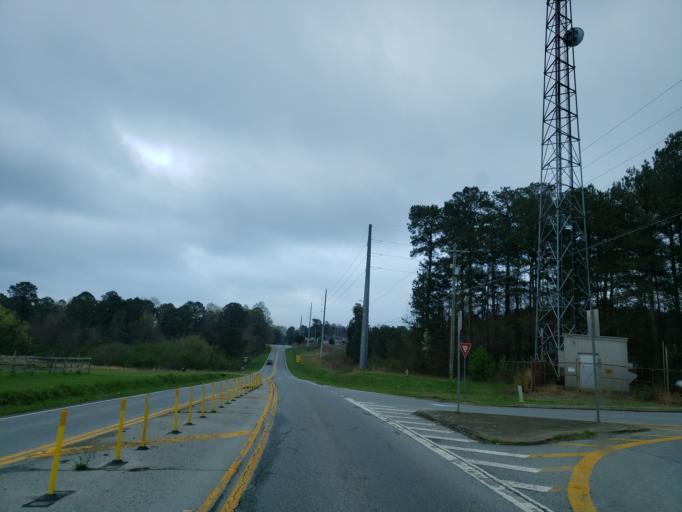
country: US
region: Georgia
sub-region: Polk County
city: Rockmart
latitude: 33.9240
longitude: -84.9906
